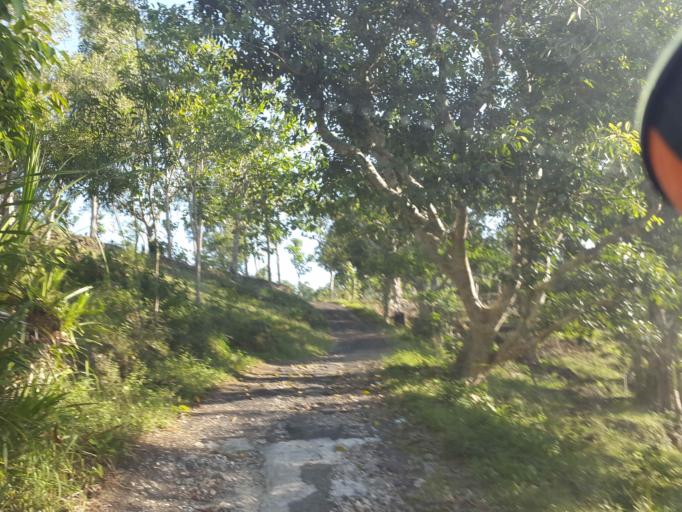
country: ID
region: Bali
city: Pejukutan
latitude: -8.7345
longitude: 115.5644
